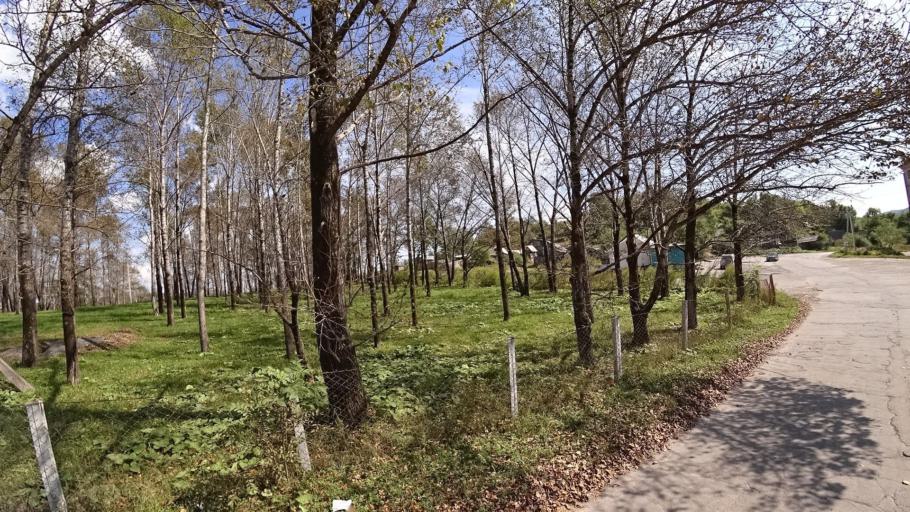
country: RU
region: Jewish Autonomous Oblast
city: Londoko
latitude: 49.0154
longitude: 131.8876
